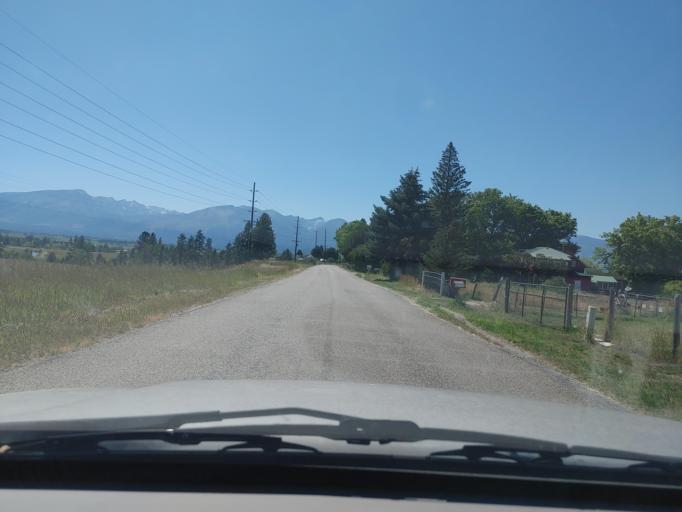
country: US
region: Montana
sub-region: Ravalli County
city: Hamilton
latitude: 46.2770
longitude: -114.0442
